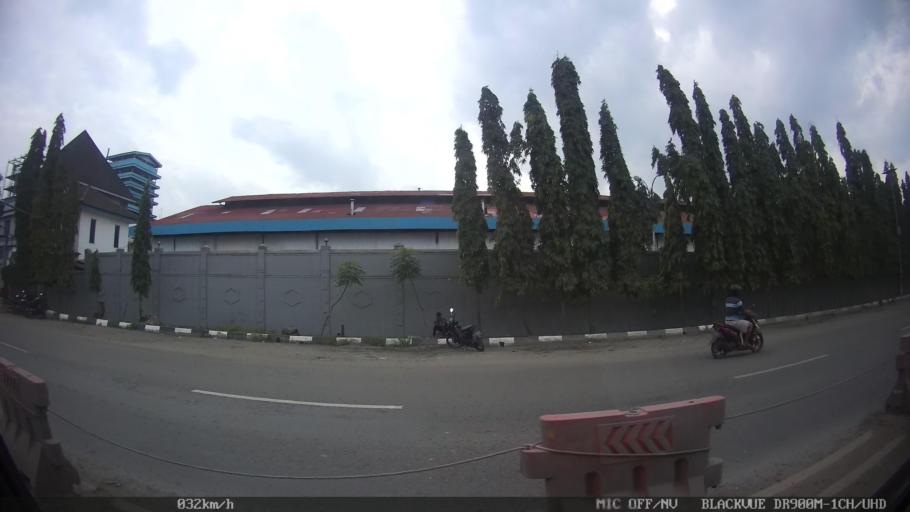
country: ID
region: Lampung
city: Panjang
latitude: -5.4574
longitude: 105.3143
